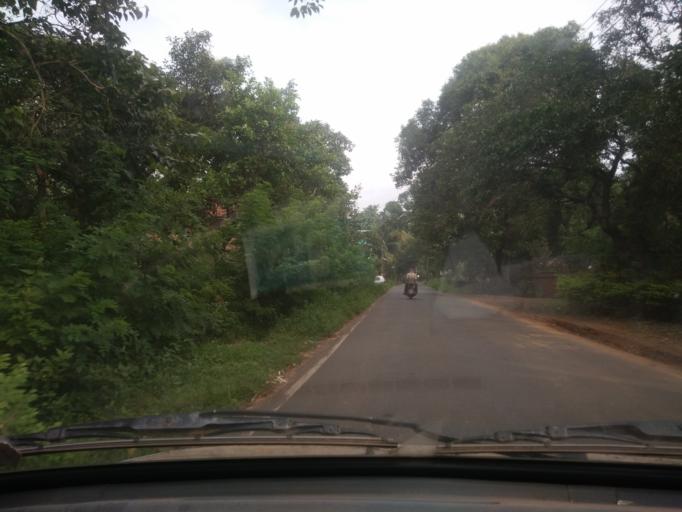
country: IN
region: Goa
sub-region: South Goa
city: Varca
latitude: 15.2238
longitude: 73.9449
